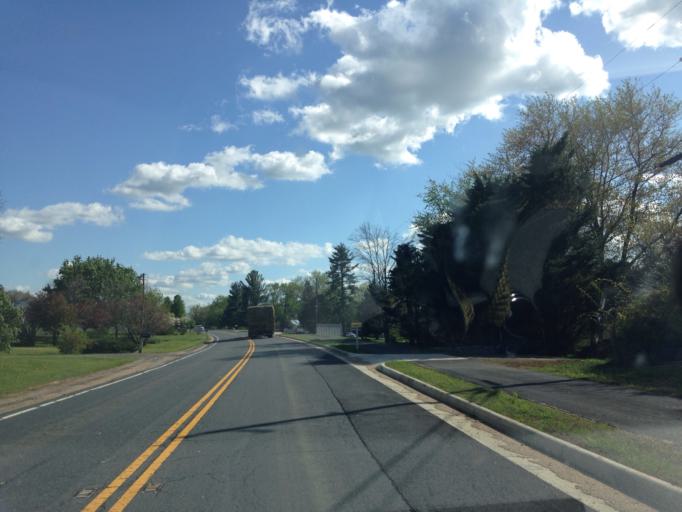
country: US
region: Virginia
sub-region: Loudoun County
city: Lovettsville
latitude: 39.2698
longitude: -77.6421
